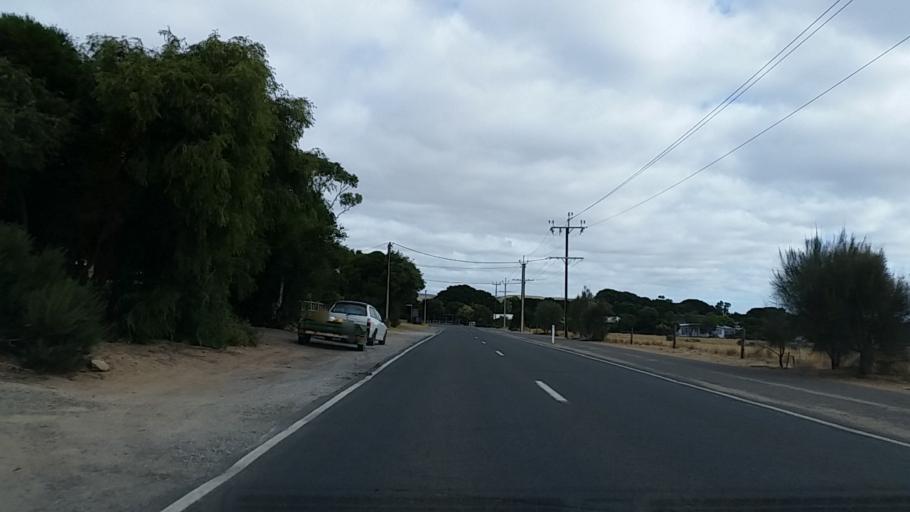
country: AU
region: South Australia
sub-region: Yankalilla
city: Normanville
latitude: -35.4427
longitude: 138.3170
